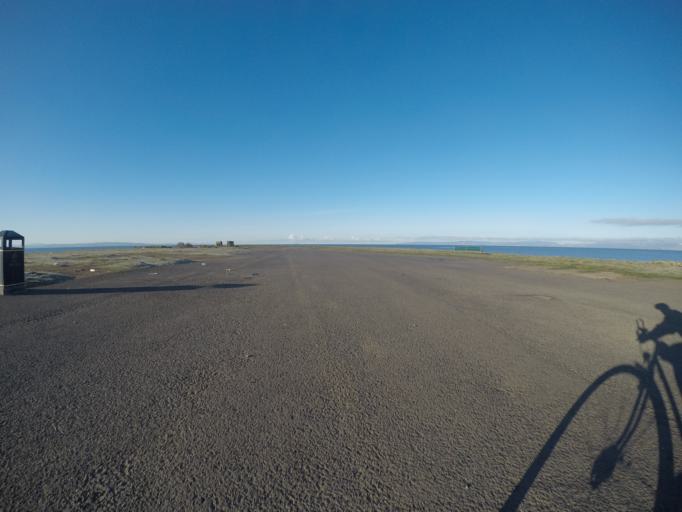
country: GB
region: Scotland
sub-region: North Ayrshire
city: Stevenston
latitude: 55.6244
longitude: -4.7489
